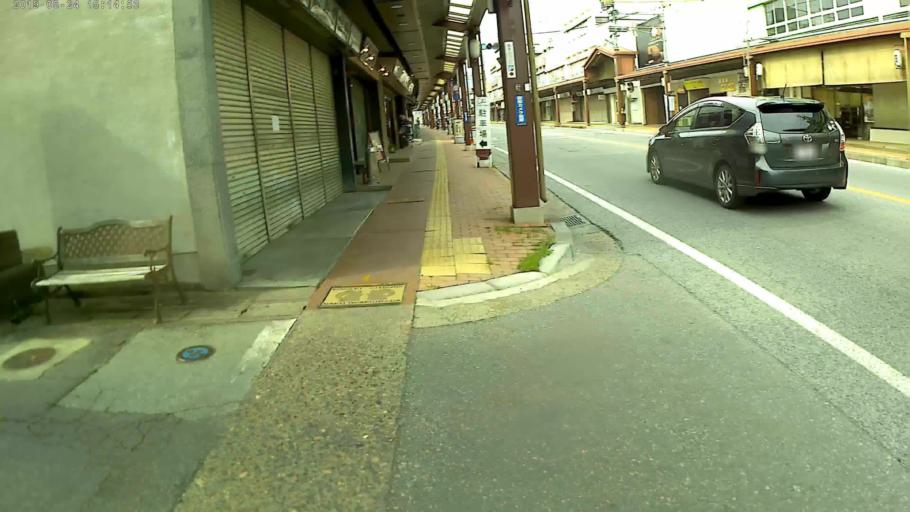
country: JP
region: Nagano
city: Saku
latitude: 36.2728
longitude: 138.4784
